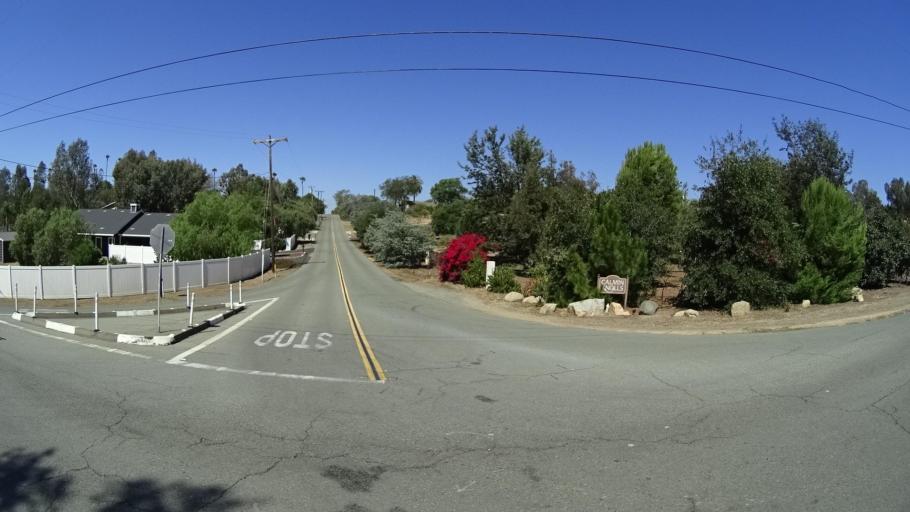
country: US
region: California
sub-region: San Diego County
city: Fallbrook
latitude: 33.3623
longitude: -117.2164
